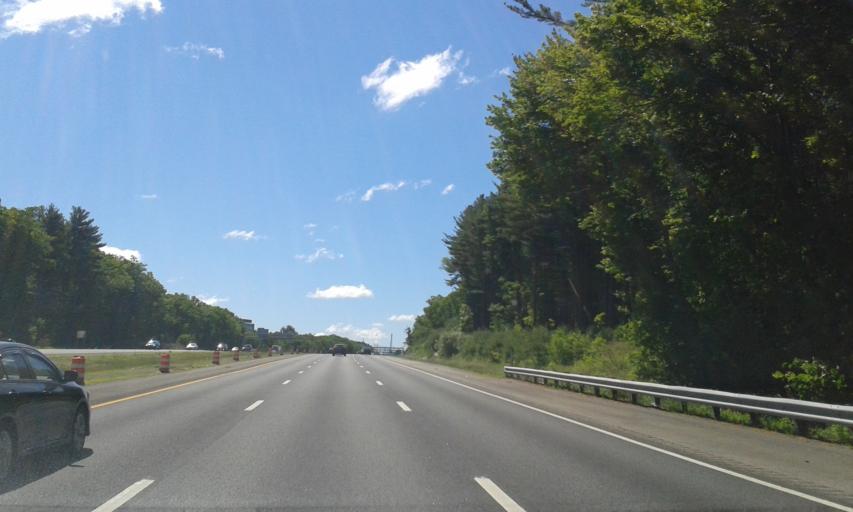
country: US
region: Massachusetts
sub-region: Middlesex County
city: Burlington
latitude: 42.4864
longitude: -71.2274
